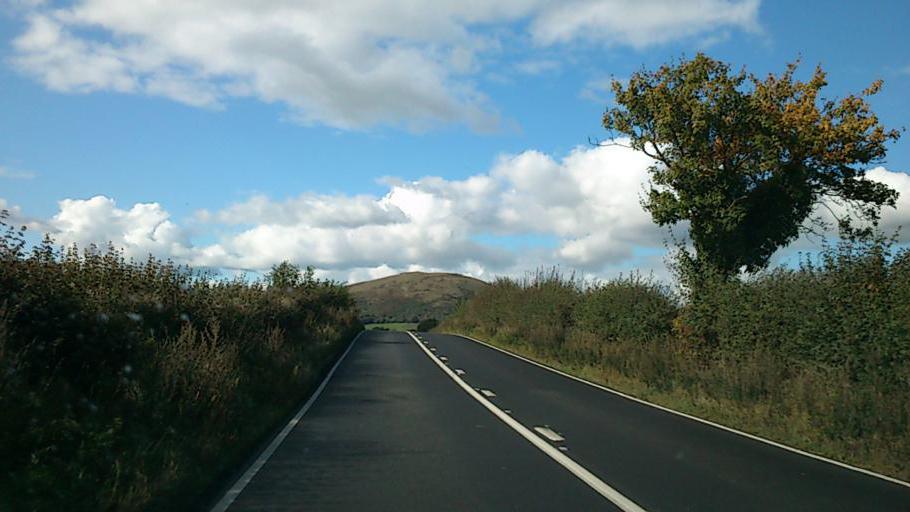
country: GB
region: England
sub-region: Shropshire
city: Westbury
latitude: 52.7026
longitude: -2.9981
